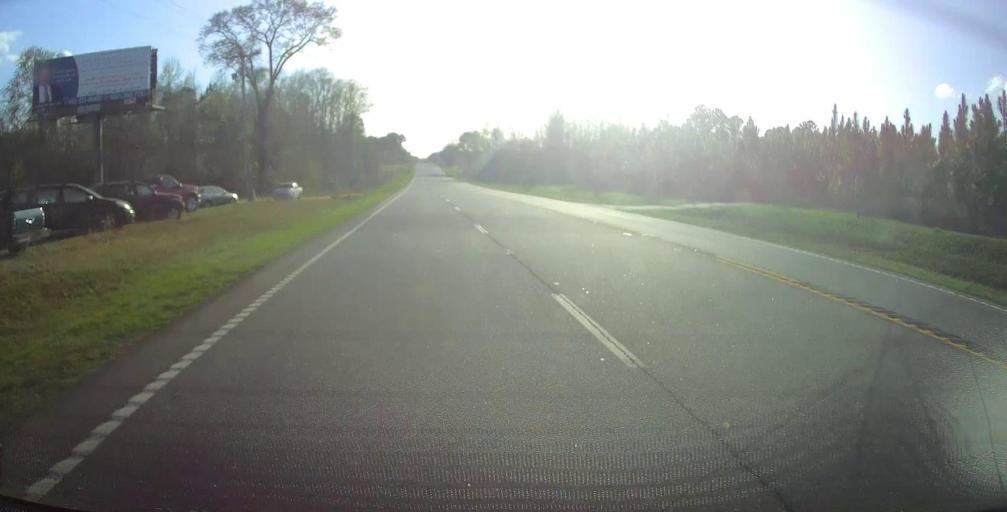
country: US
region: Georgia
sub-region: Tattnall County
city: Reidsville
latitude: 32.1093
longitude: -82.0869
